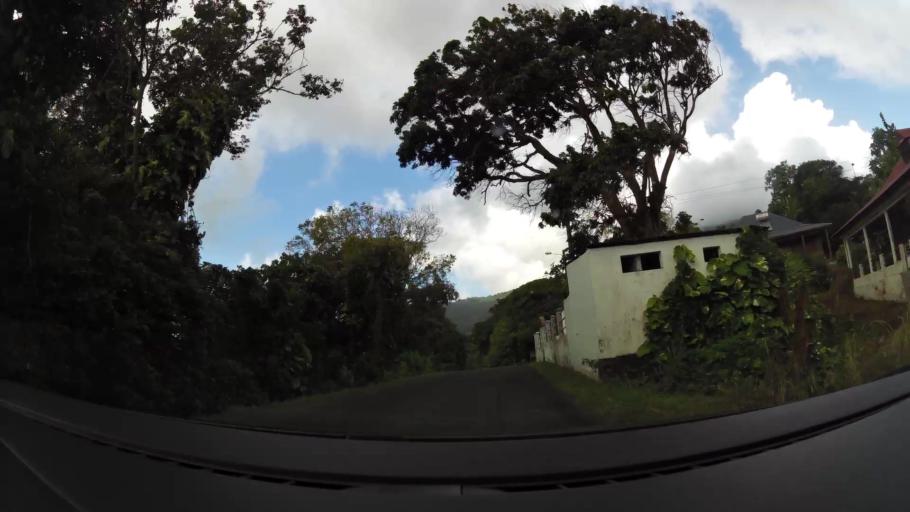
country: GP
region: Guadeloupe
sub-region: Guadeloupe
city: Trois-Rivieres
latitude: 15.9829
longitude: -61.6336
